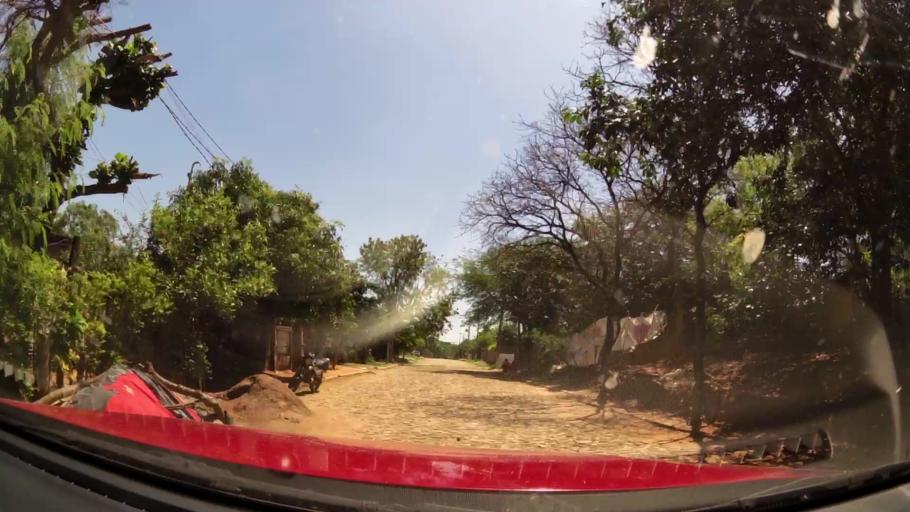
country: PY
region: Central
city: Colonia Mariano Roque Alonso
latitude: -25.2370
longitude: -57.5522
